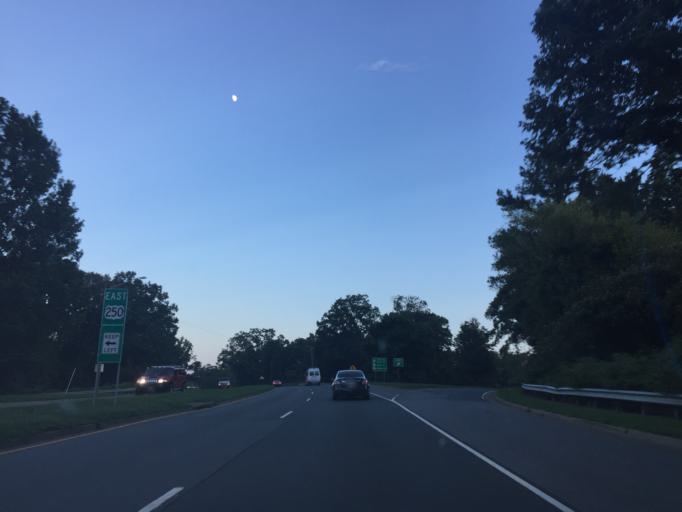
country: US
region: Virginia
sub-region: City of Charlottesville
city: Charlottesville
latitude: 38.0470
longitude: -78.4796
